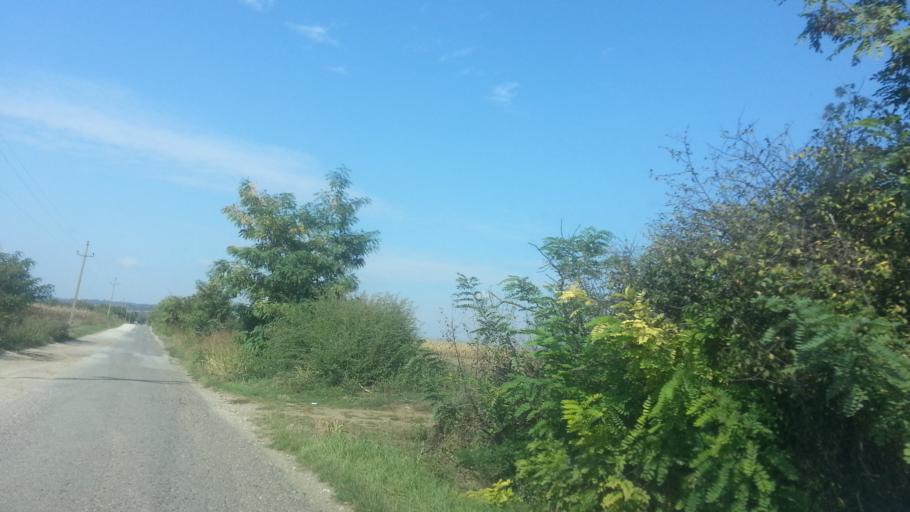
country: RS
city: Novi Slankamen
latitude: 45.1235
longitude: 20.2636
